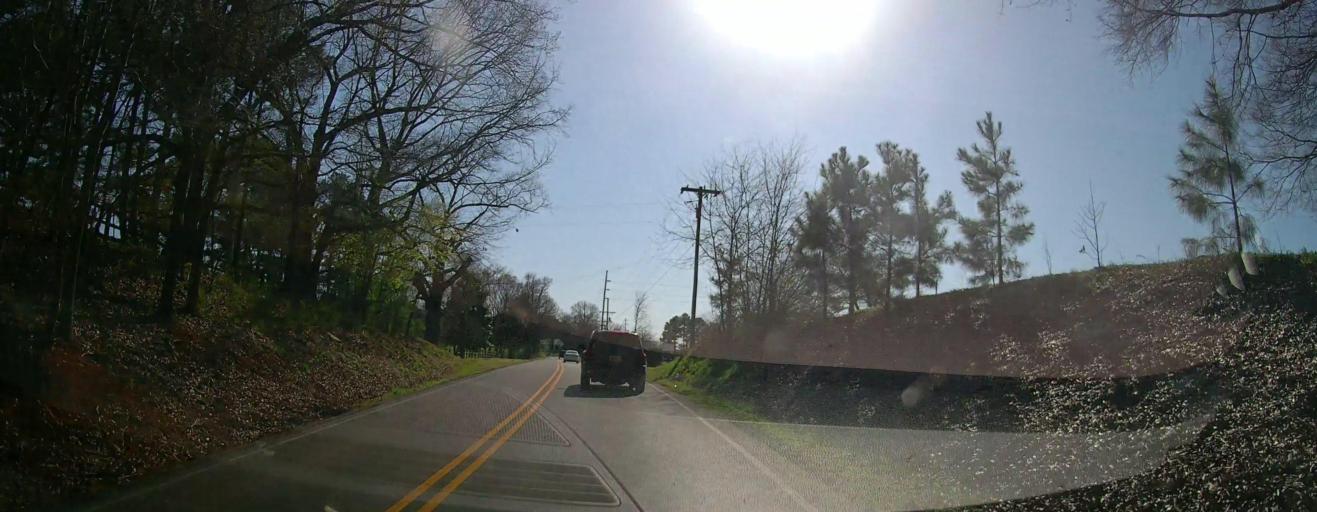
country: US
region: Alabama
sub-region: Lauderdale County
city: East Florence
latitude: 34.8321
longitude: -87.6133
